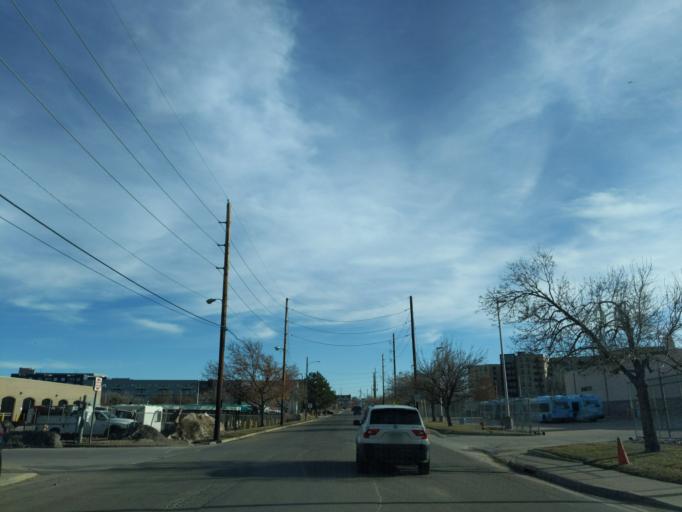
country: US
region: Colorado
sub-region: Denver County
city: Denver
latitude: 39.7692
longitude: -104.9871
